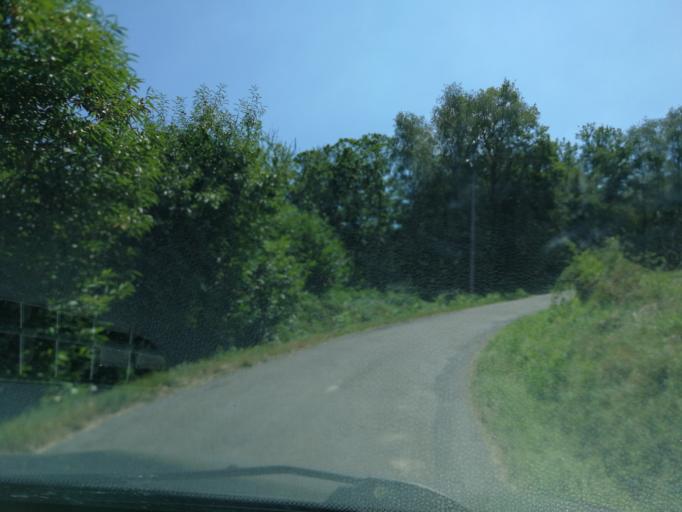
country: FR
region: Auvergne
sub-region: Departement du Cantal
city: Maurs
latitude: 44.6829
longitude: 2.3258
